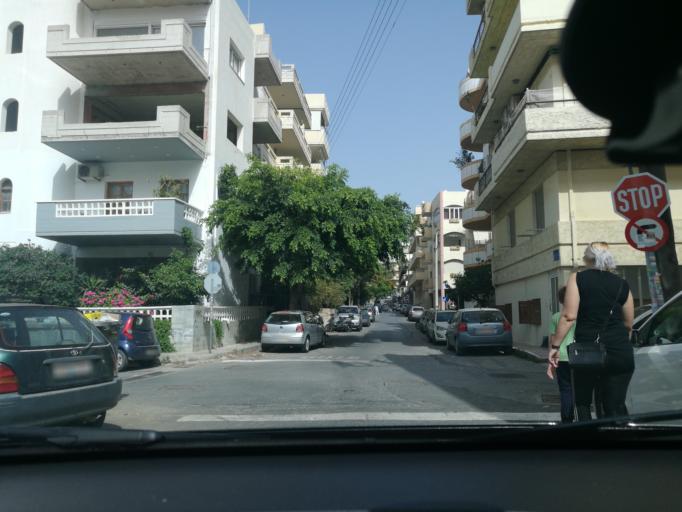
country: GR
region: Crete
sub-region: Nomos Irakleiou
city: Irakleion
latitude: 35.3287
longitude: 25.1315
